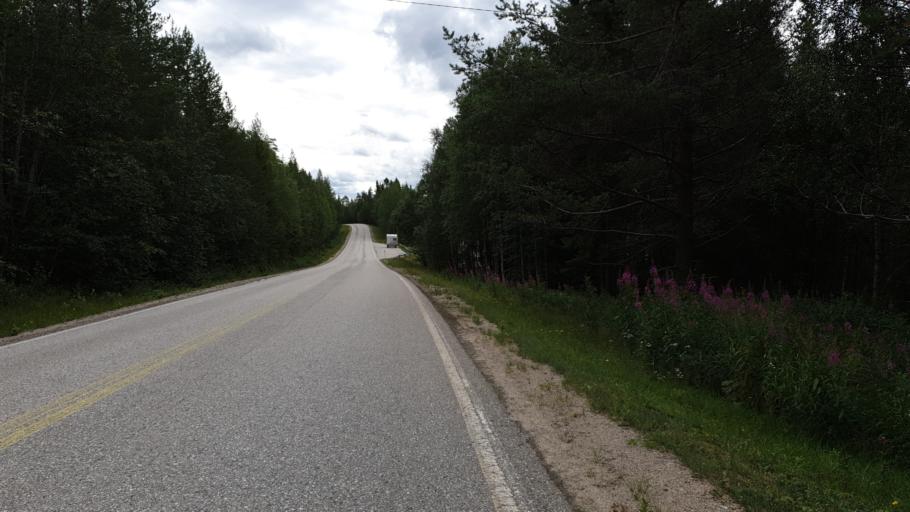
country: FI
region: Kainuu
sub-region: Kehys-Kainuu
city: Kuhmo
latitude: 64.4563
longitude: 29.7699
